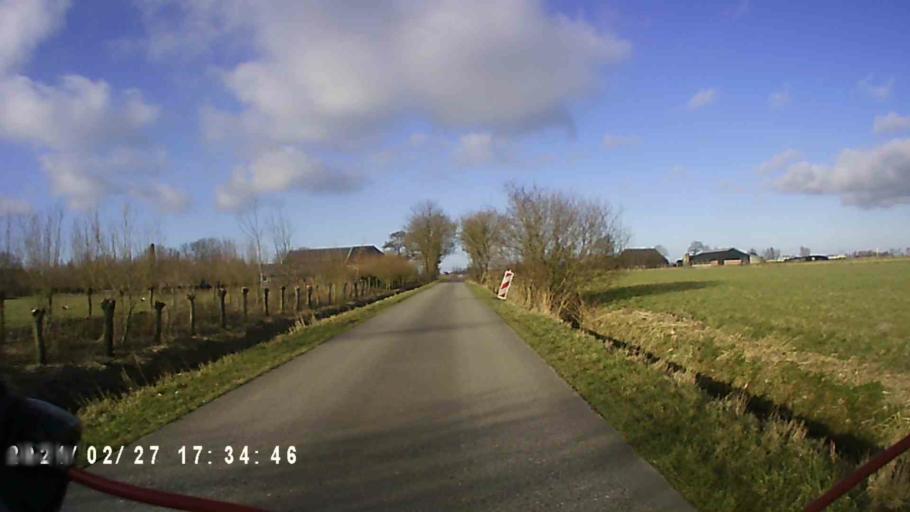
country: NL
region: Groningen
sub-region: Gemeente Bedum
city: Bedum
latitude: 53.3335
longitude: 6.5696
